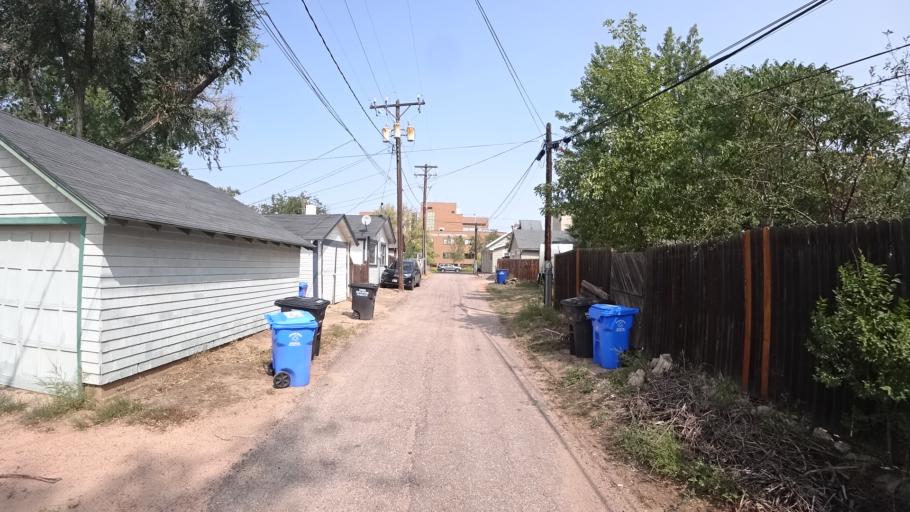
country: US
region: Colorado
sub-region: El Paso County
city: Colorado Springs
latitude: 38.8381
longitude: -104.7998
